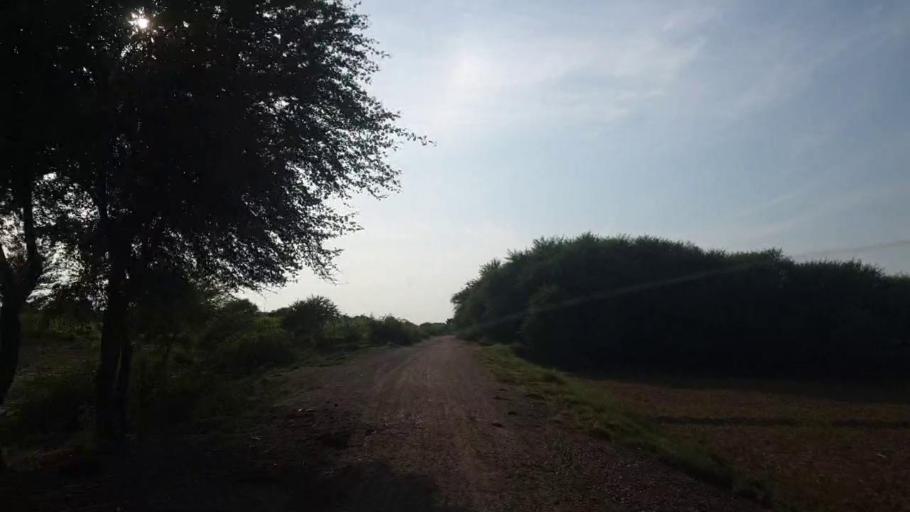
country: PK
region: Sindh
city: Tando Muhammad Khan
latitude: 25.2294
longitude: 68.5380
